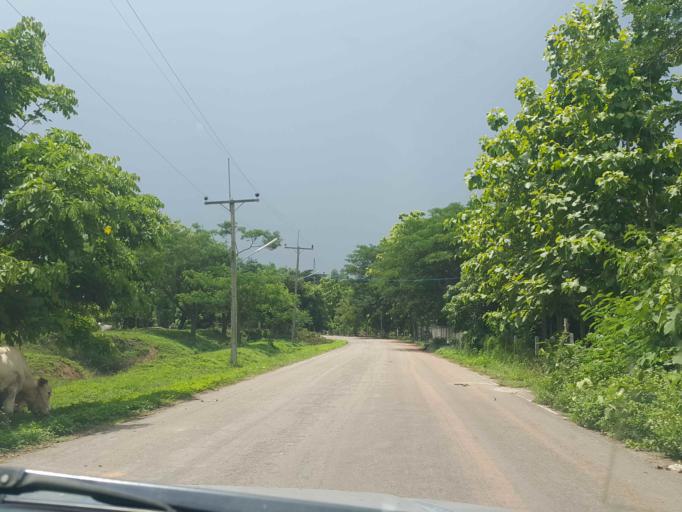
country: TH
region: Phayao
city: Dok Kham Tai
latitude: 19.0525
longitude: 99.9468
